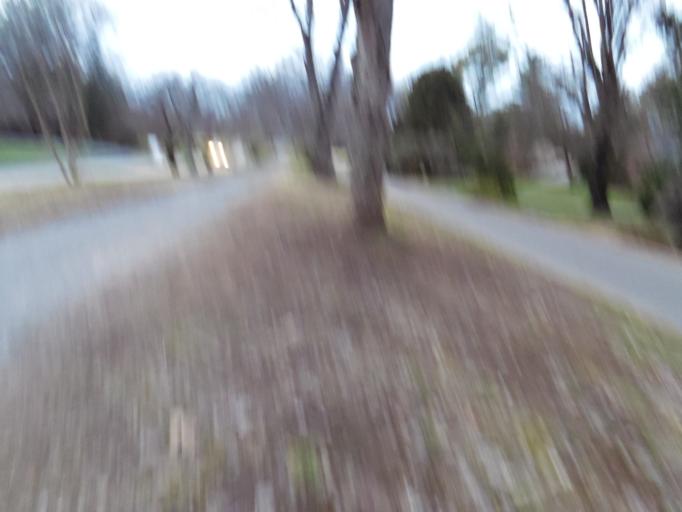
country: US
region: Tennessee
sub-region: Knox County
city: Knoxville
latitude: 35.9292
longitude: -83.9716
